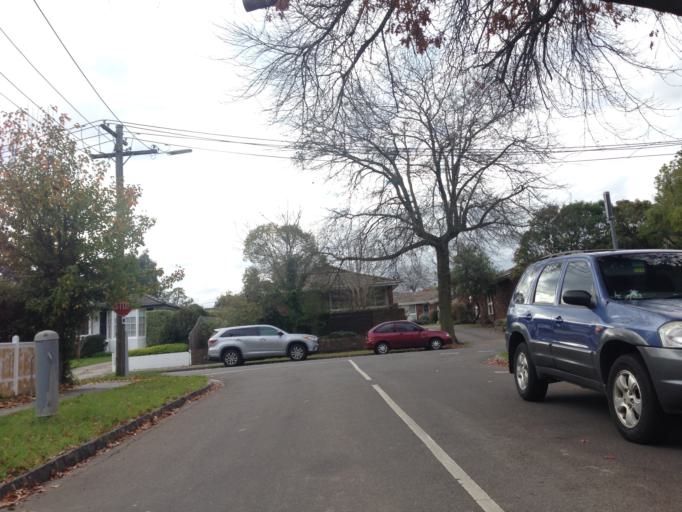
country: AU
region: Victoria
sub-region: Boroondara
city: Kew East
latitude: -37.7947
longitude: 145.0650
